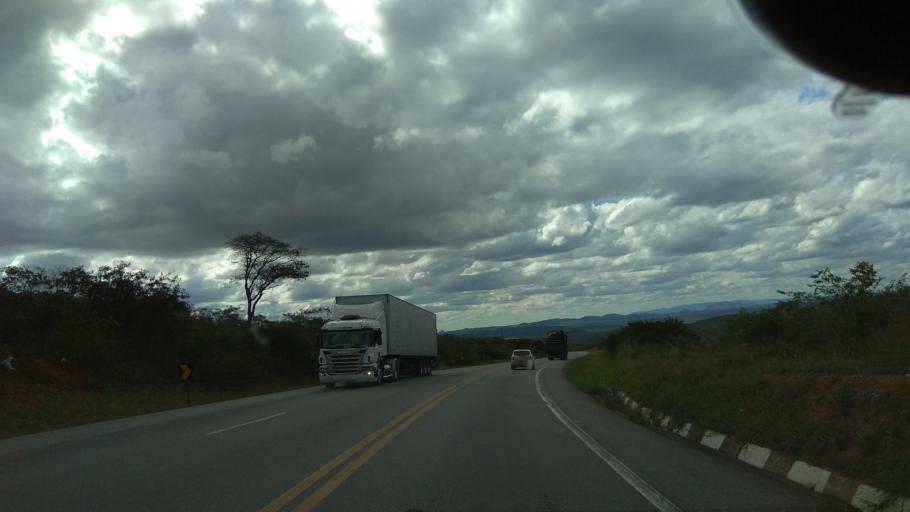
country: BR
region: Bahia
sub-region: Santa Ines
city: Santa Ines
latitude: -13.0525
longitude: -39.9601
